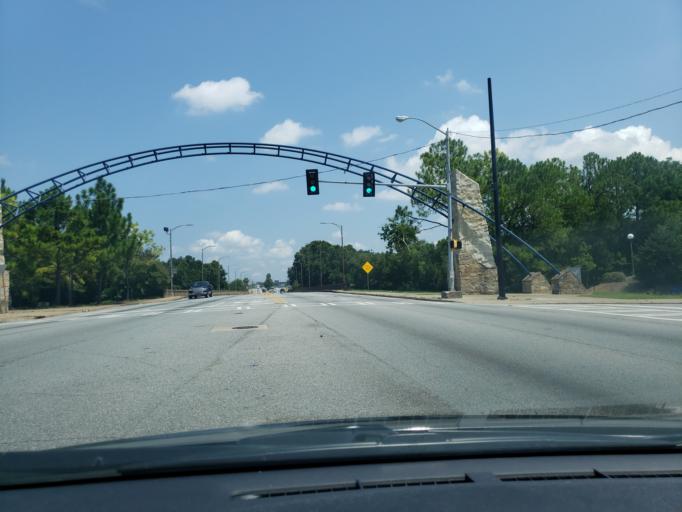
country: US
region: Georgia
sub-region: Dougherty County
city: Albany
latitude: 31.5753
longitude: -84.1492
